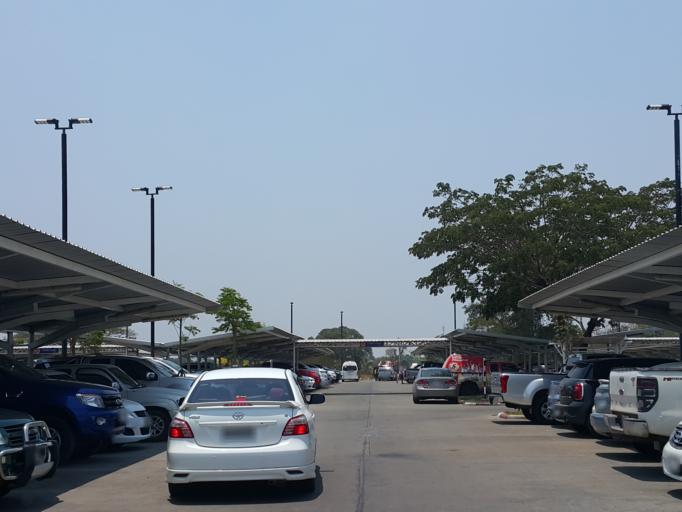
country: TH
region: Phitsanulok
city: Phitsanulok
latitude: 16.8402
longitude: 100.2318
